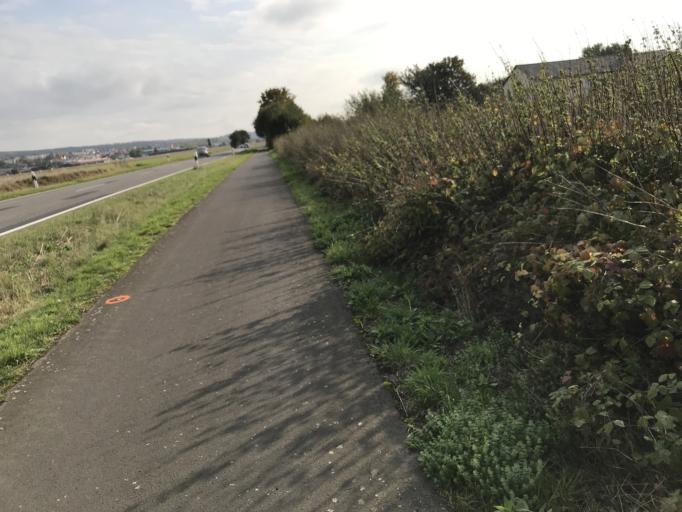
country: DE
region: Hesse
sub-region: Regierungsbezirk Giessen
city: Langgons
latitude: 50.5109
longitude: 8.6543
